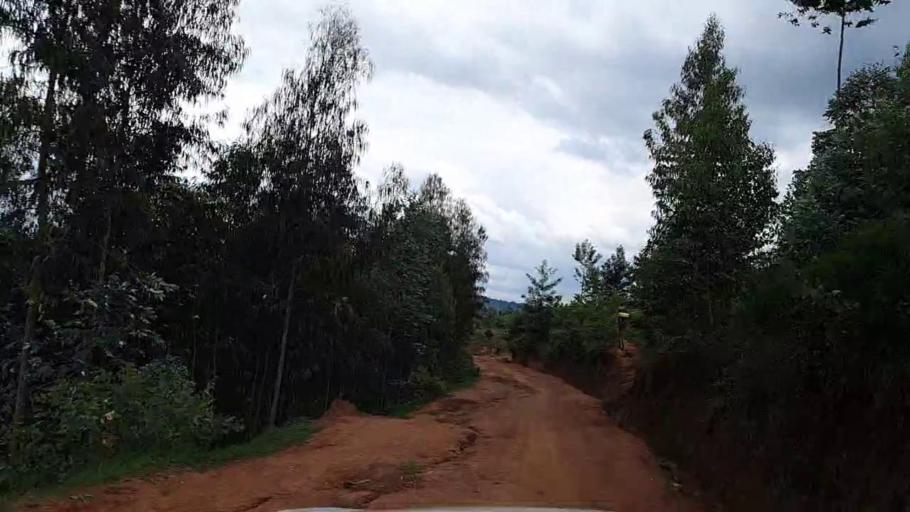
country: RW
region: Southern Province
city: Gikongoro
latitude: -2.4209
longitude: 29.6511
